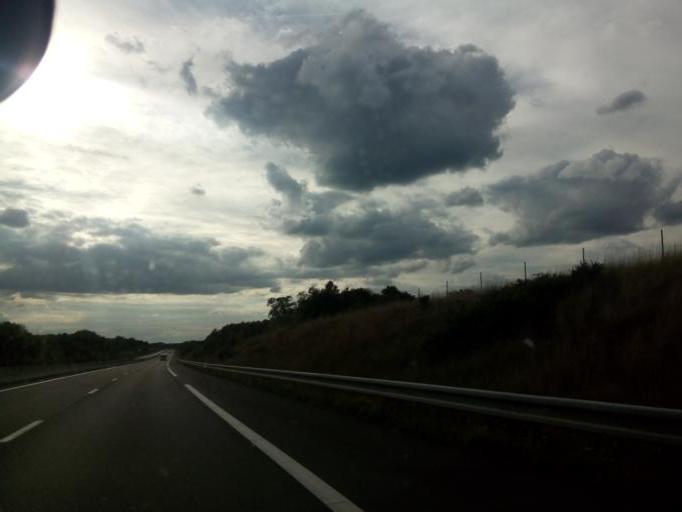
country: FR
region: Centre
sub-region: Departement du Loir-et-Cher
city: Faverolles-sur-Cher
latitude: 47.2936
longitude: 1.1741
